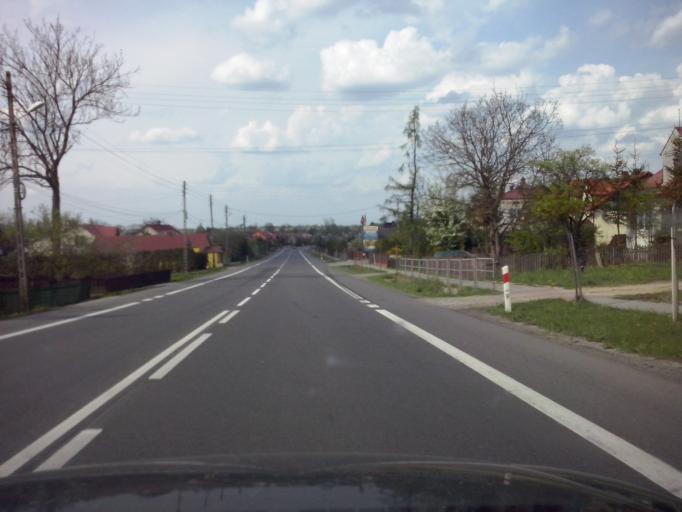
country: PL
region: Subcarpathian Voivodeship
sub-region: Powiat rzeszowski
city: Gorno
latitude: 50.3098
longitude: 22.1313
